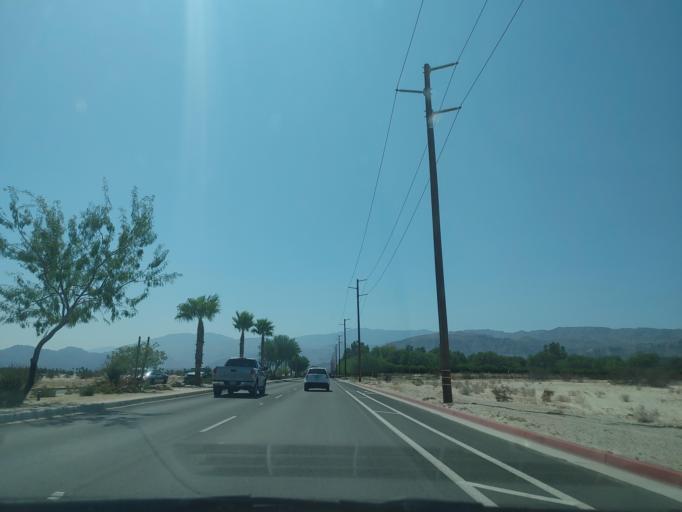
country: US
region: California
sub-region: Riverside County
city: Thousand Palms
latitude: 33.7826
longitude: -116.4062
